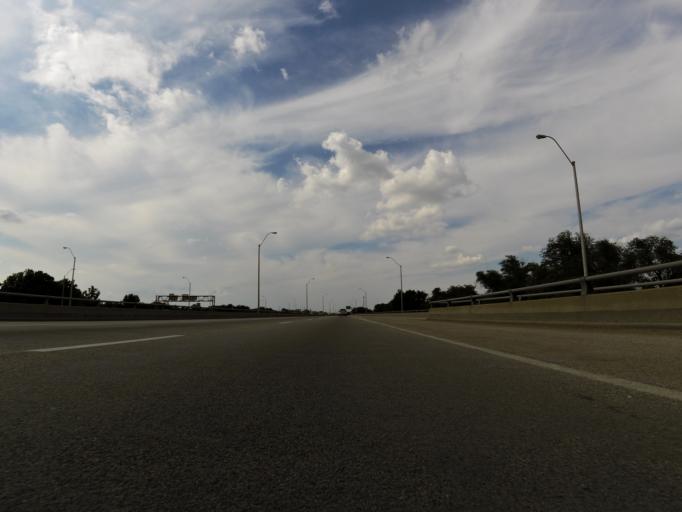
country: US
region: Kansas
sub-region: Sedgwick County
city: Wichita
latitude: 37.7096
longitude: -97.3201
